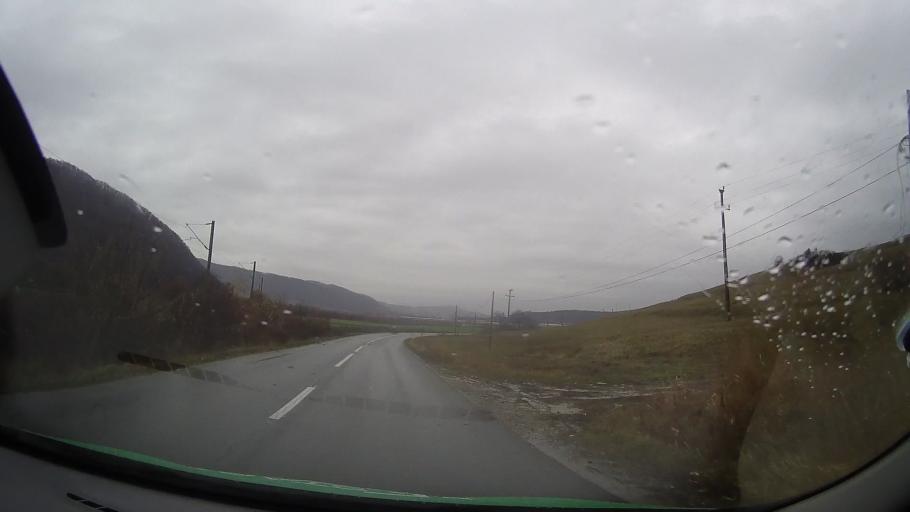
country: RO
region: Bistrita-Nasaud
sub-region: Municipiul Bistrita
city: Viisoara
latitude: 47.0568
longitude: 24.4404
